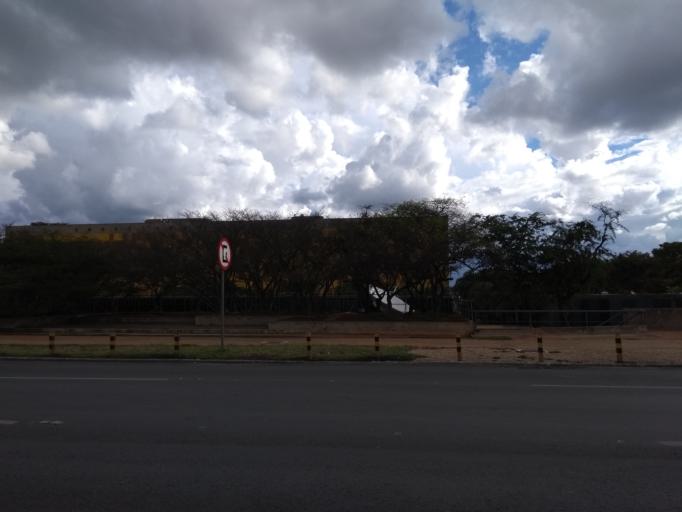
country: BR
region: Federal District
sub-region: Brasilia
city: Brasilia
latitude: -15.8002
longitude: -47.8656
